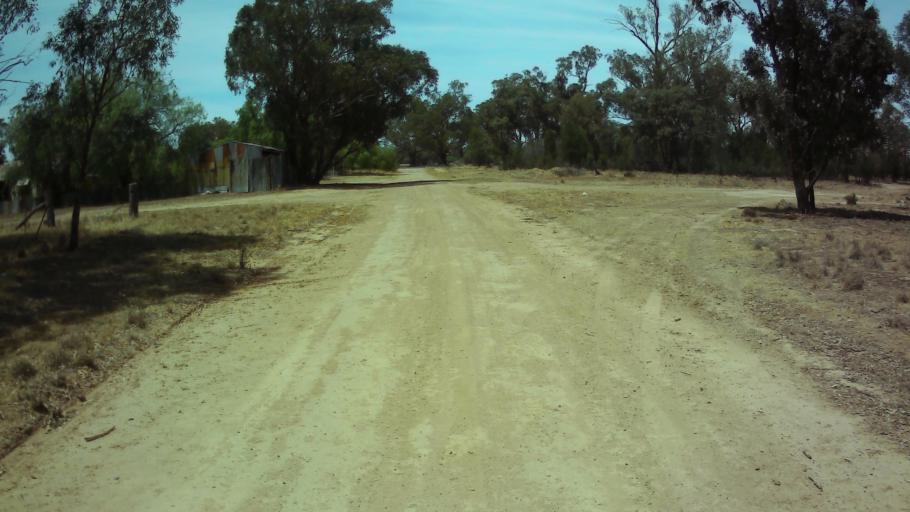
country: AU
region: New South Wales
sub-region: Weddin
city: Grenfell
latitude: -34.0363
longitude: 147.9239
